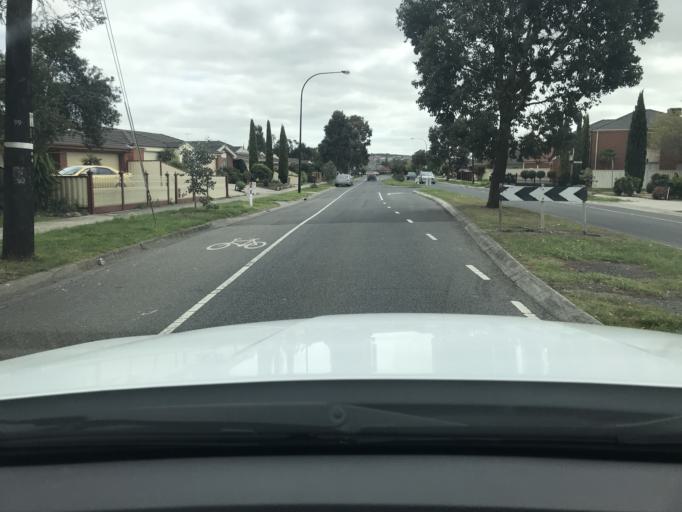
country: AU
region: Victoria
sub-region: Hume
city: Craigieburn
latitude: -37.5901
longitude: 144.9368
